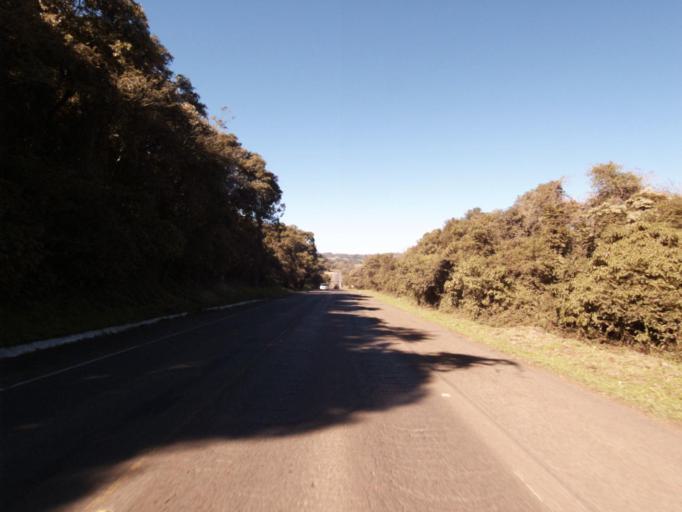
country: BR
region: Santa Catarina
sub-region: Sao Lourenco Do Oeste
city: Sao Lourenco dOeste
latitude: -26.7949
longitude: -53.1933
